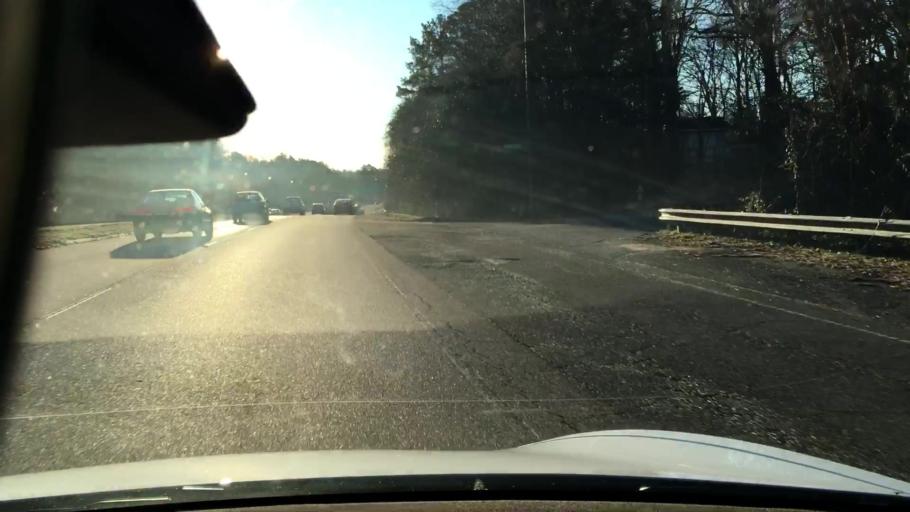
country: US
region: Virginia
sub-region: Chesterfield County
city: Bon Air
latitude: 37.5414
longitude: -77.5343
